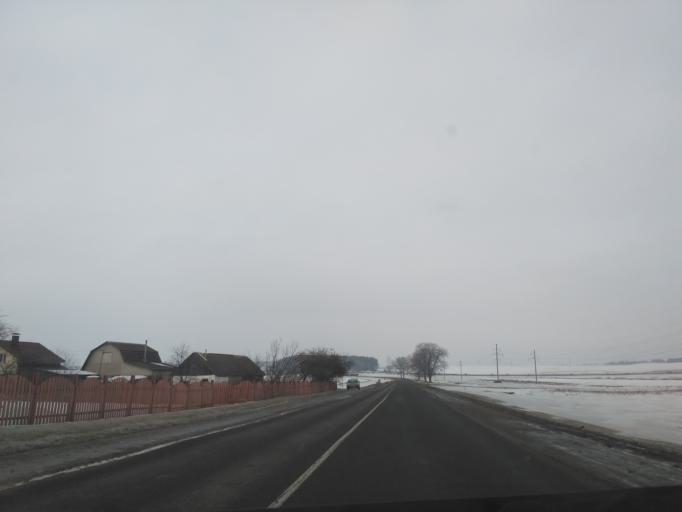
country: BY
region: Minsk
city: Horad Smalyavichy
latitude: 54.0327
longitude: 28.0574
